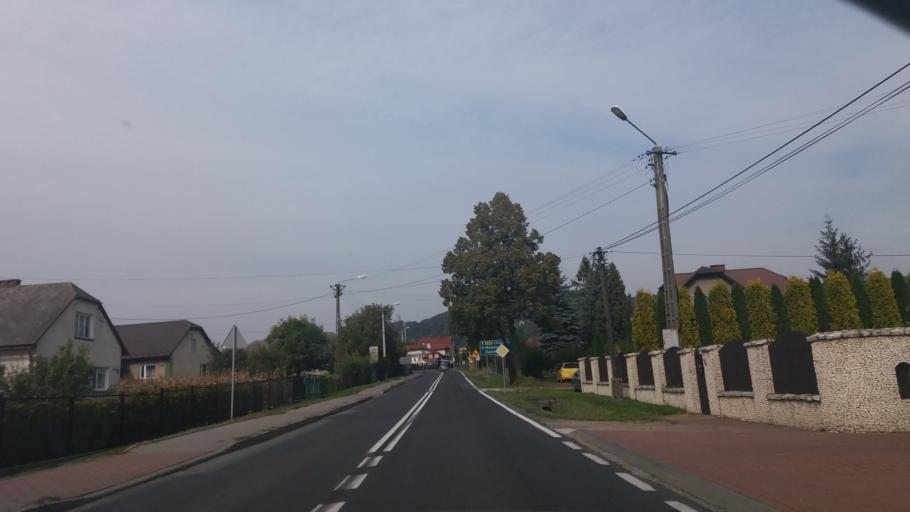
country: PL
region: Lesser Poland Voivodeship
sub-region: Powiat chrzanowski
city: Babice
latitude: 50.0644
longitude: 19.4518
